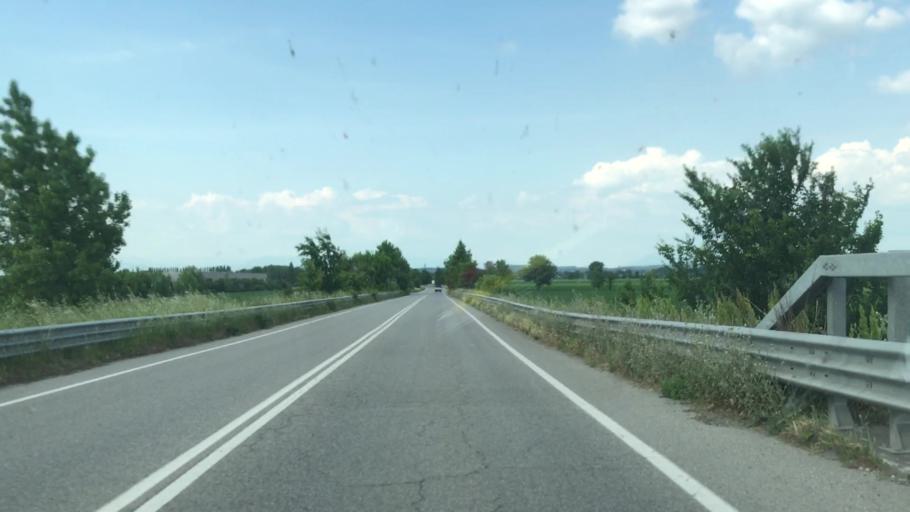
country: IT
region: Lombardy
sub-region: Provincia di Mantova
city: Castel Goffredo
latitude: 45.3005
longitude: 10.4921
